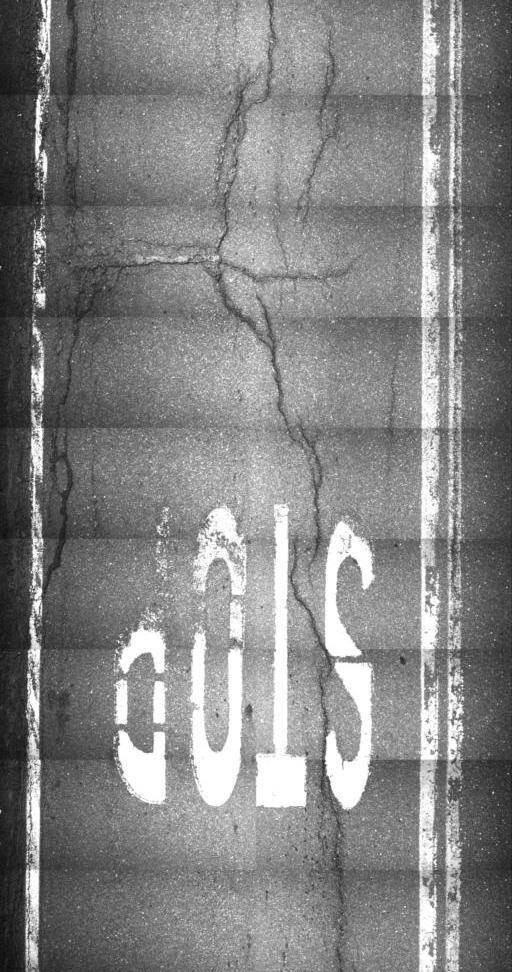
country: US
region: Vermont
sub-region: Windham County
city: Rockingham
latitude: 43.1785
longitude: -72.4604
